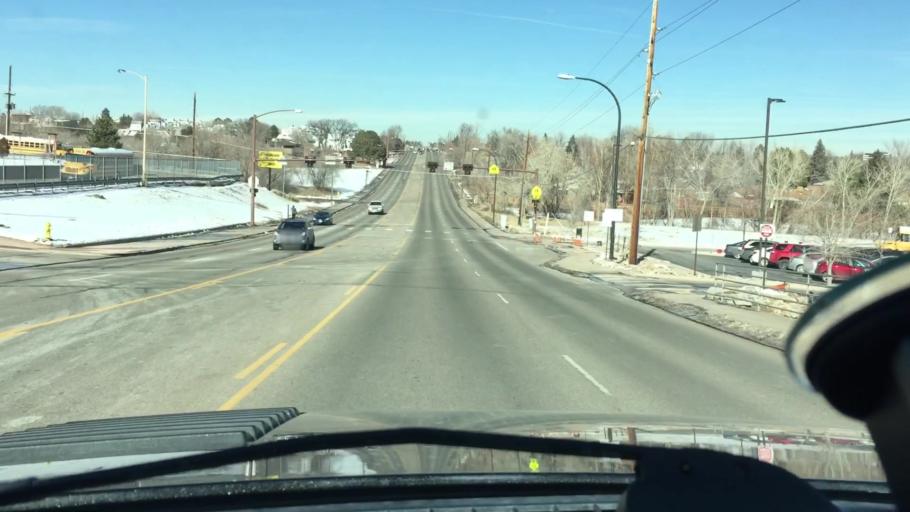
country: US
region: Colorado
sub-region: Adams County
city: Federal Heights
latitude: 39.8498
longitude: -104.9966
